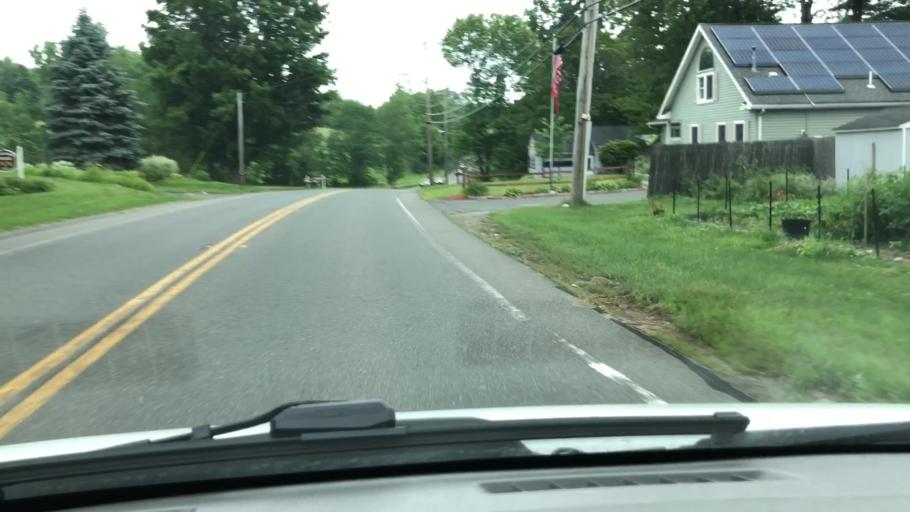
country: US
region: Massachusetts
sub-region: Berkshire County
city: Adams
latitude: 42.5771
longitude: -73.1515
